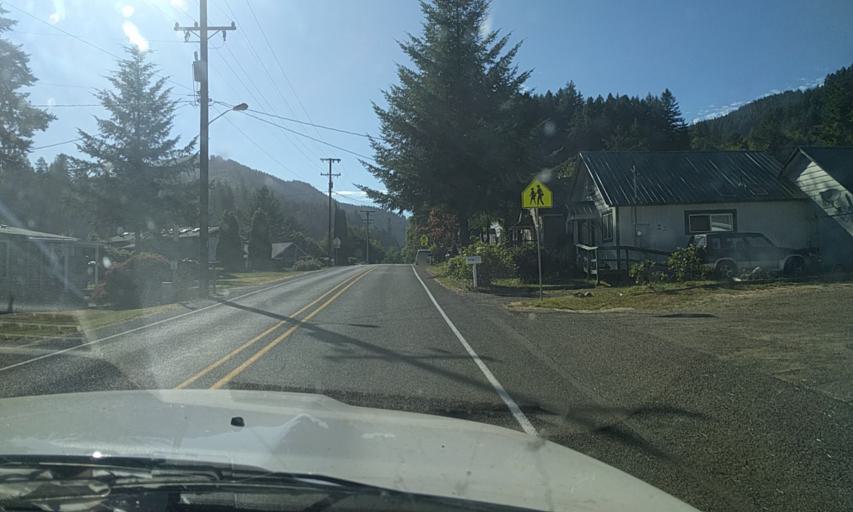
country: US
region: Oregon
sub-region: Lane County
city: Florence
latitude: 44.0358
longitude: -123.8567
